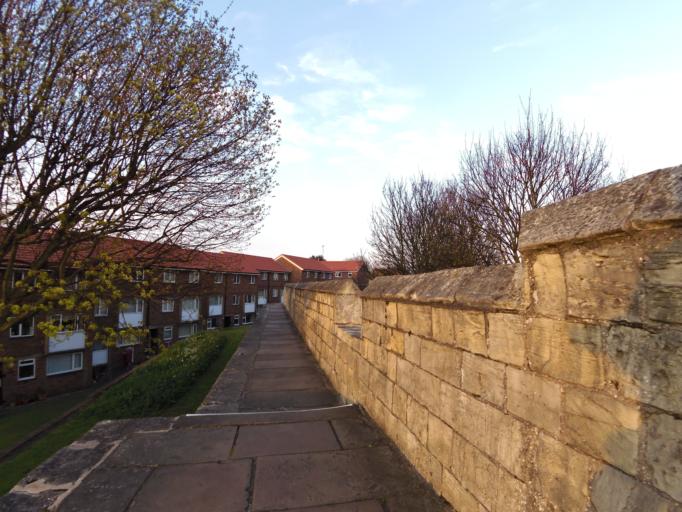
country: GB
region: England
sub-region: City of York
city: York
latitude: 53.9539
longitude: -1.0766
